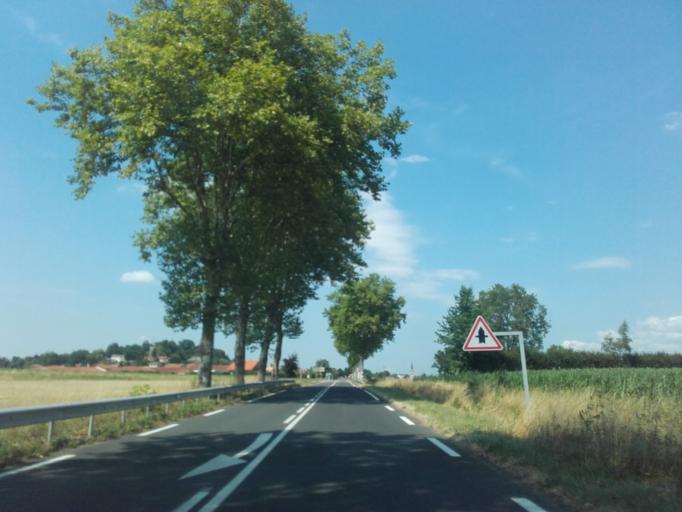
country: FR
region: Rhone-Alpes
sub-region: Departement de l'Ain
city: Chalamont
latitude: 45.9877
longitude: 5.1677
